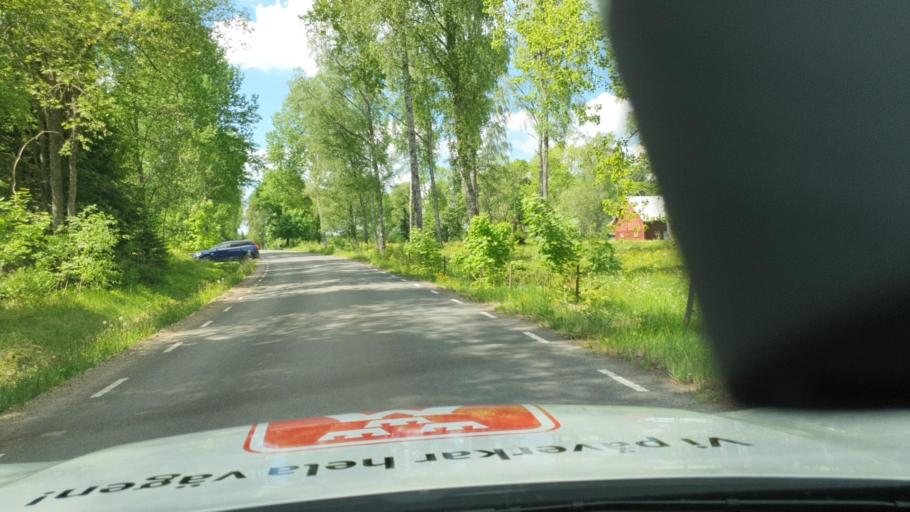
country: SE
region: Joenkoeping
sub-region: Mullsjo Kommun
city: Mullsjoe
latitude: 58.0087
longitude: 13.7170
